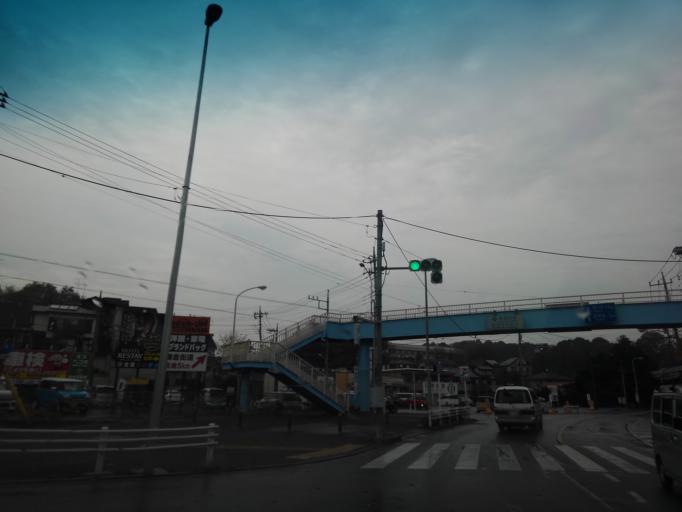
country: JP
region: Tokyo
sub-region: Machida-shi
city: Machida
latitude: 35.5724
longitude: 139.4431
